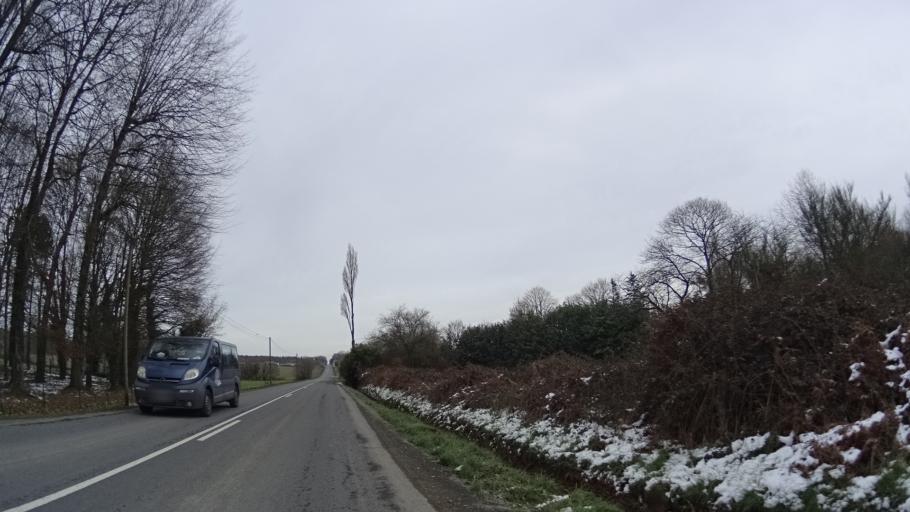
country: FR
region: Brittany
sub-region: Departement d'Ille-et-Vilaine
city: Montauban-de-Bretagne
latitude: 48.2120
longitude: -2.0341
